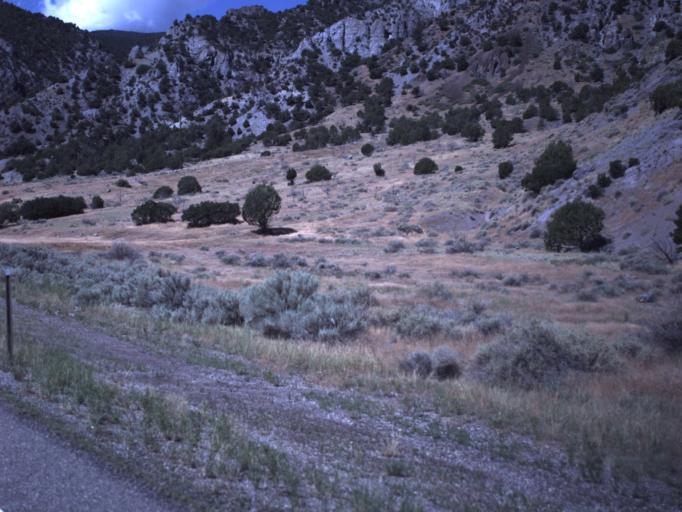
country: US
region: Utah
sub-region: Sevier County
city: Monroe
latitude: 38.5374
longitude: -112.2671
